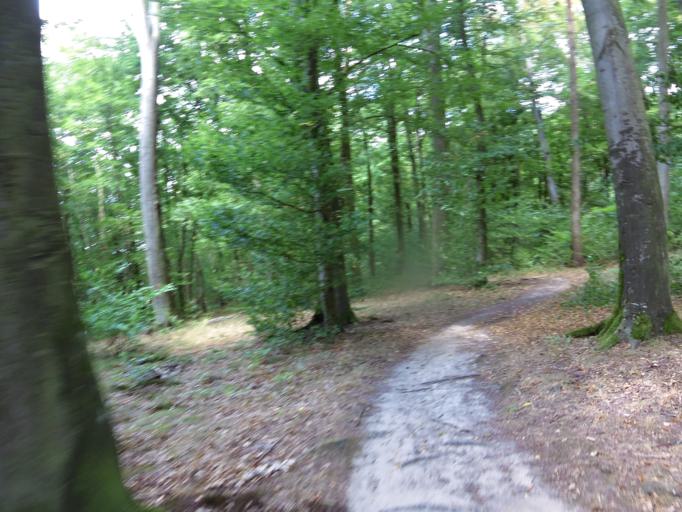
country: DE
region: Bavaria
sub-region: Regierungsbezirk Unterfranken
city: Waldbuttelbrunn
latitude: 49.7846
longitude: 9.8538
